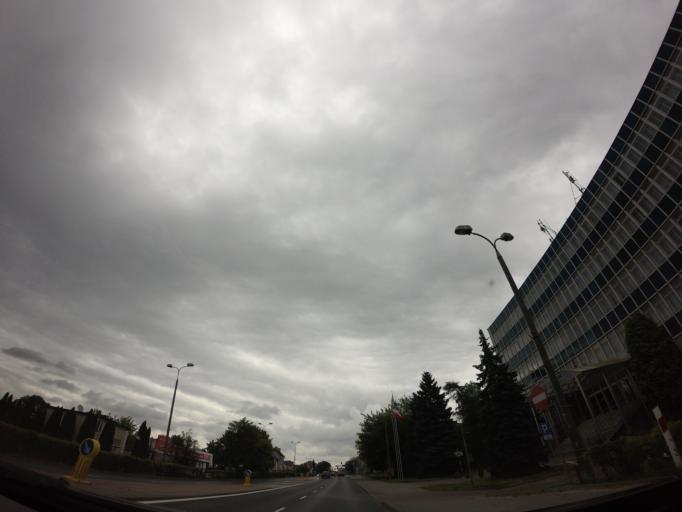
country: PL
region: Masovian Voivodeship
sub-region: Powiat ciechanowski
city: Ciechanow
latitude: 52.8817
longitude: 20.6158
